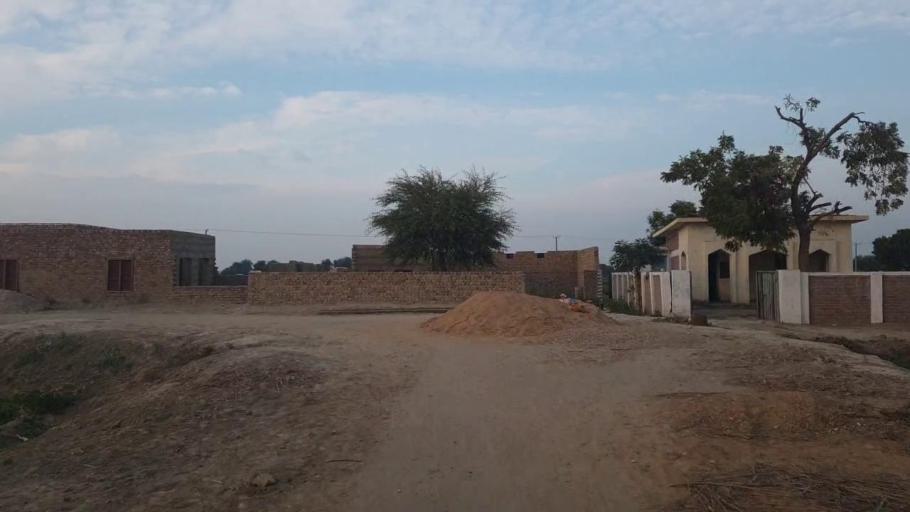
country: PK
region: Sindh
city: Shahpur Chakar
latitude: 26.0925
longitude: 68.5373
